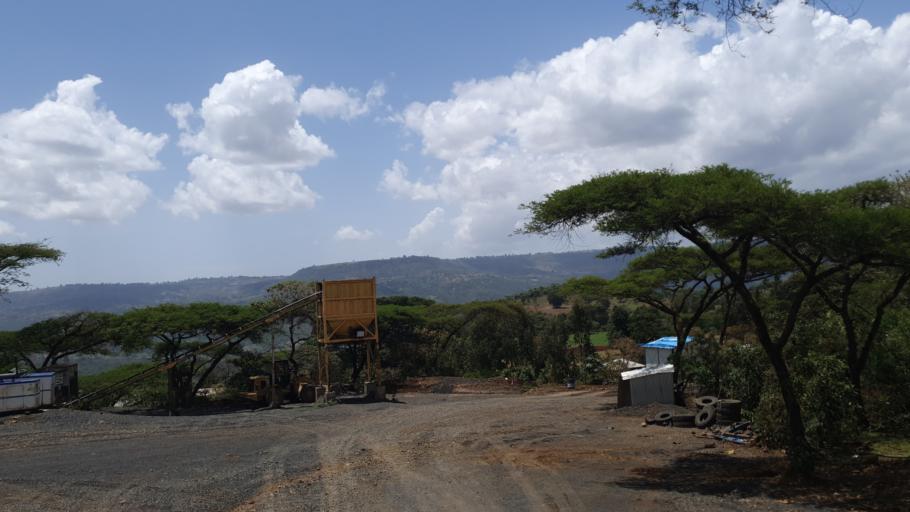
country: ET
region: Oromiya
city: Shambu
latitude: 10.0234
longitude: 36.8829
